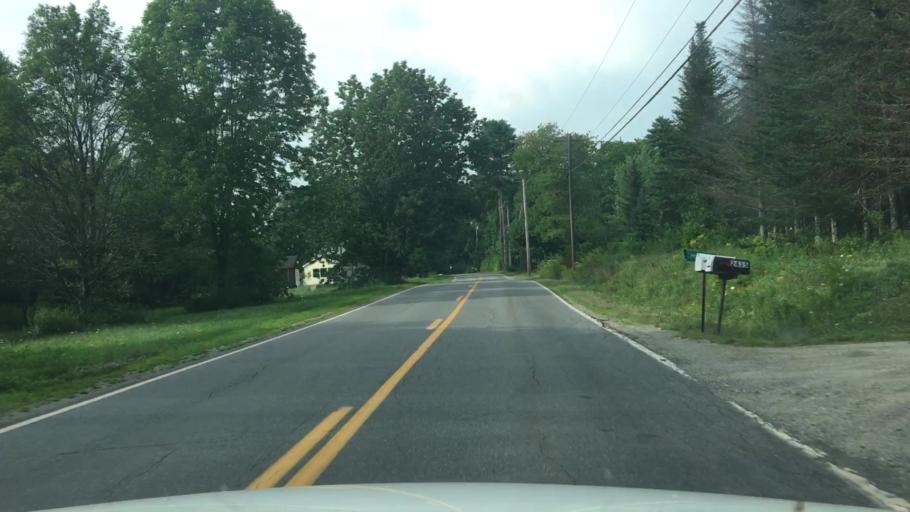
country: US
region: Maine
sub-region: Lincoln County
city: Waldoboro
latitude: 44.1679
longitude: -69.3779
